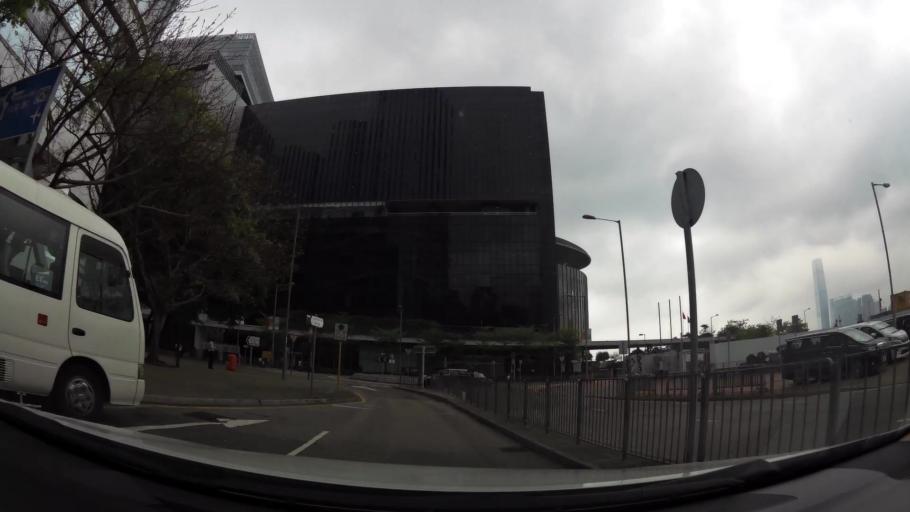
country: HK
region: Wanchai
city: Wan Chai
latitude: 22.2810
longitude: 114.1673
